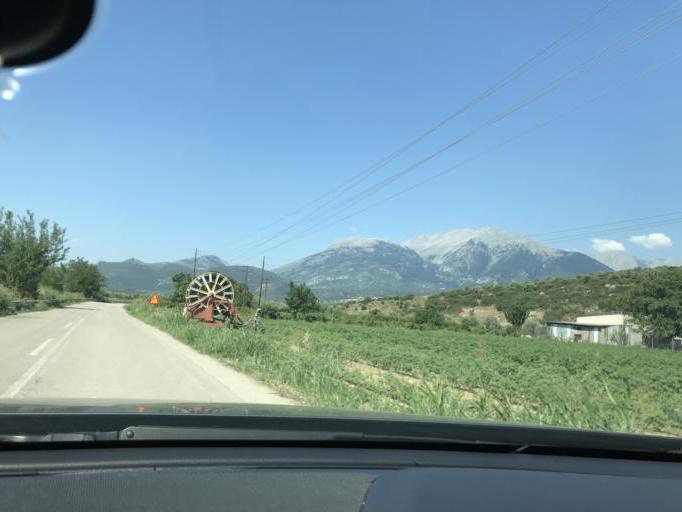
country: GR
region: Central Greece
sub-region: Nomos Fthiotidos
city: Elateia
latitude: 38.5265
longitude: 22.7959
